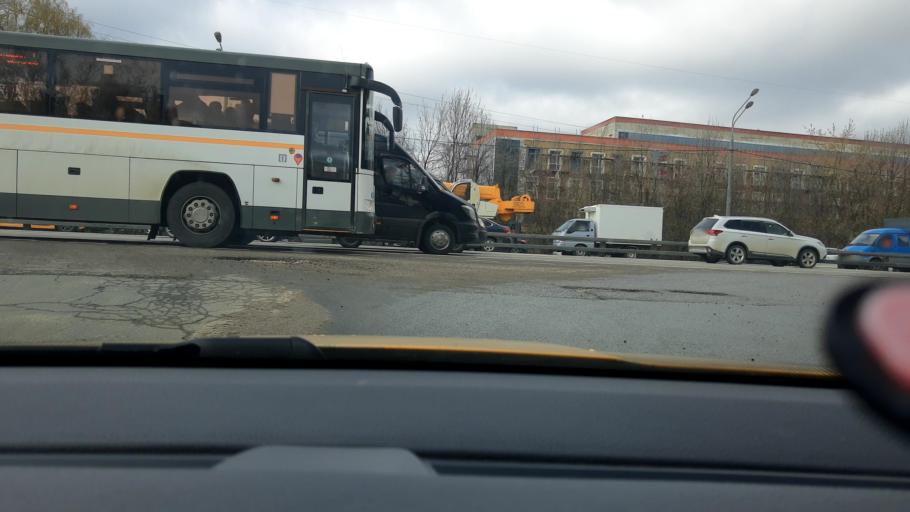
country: RU
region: Moscow
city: Khimki
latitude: 55.8945
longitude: 37.4295
